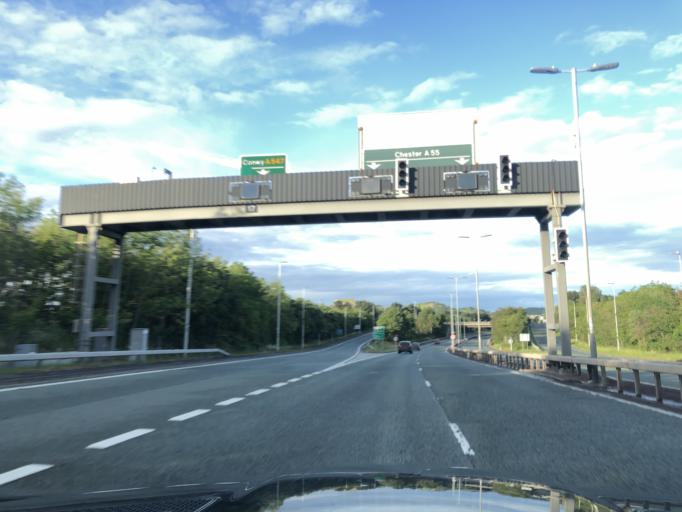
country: GB
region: Wales
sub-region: Conwy
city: Conwy
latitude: 53.2881
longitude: -3.8569
